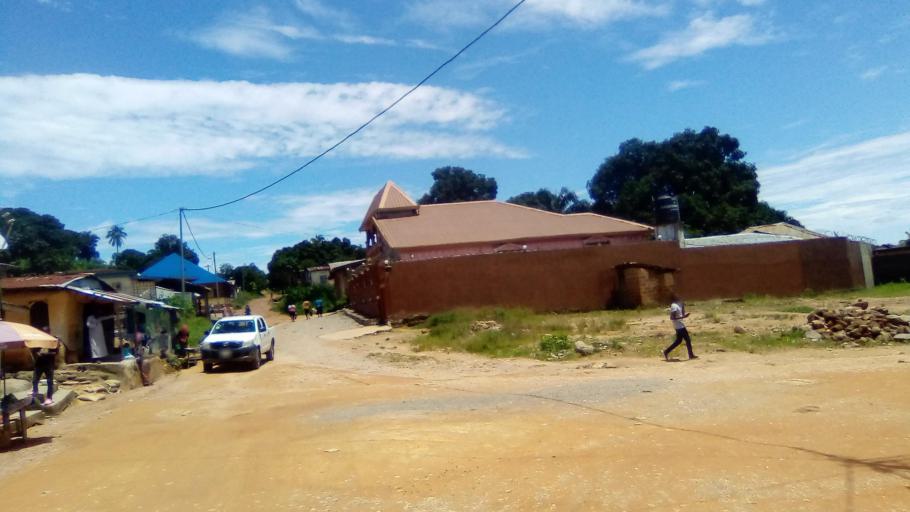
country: SL
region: Eastern Province
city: Koidu
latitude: 8.6393
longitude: -10.9827
